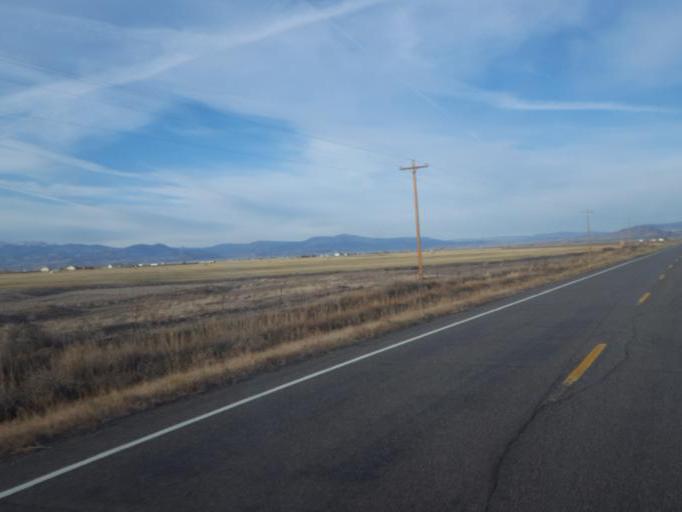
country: US
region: Colorado
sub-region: Saguache County
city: Center
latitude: 37.7482
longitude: -106.1763
